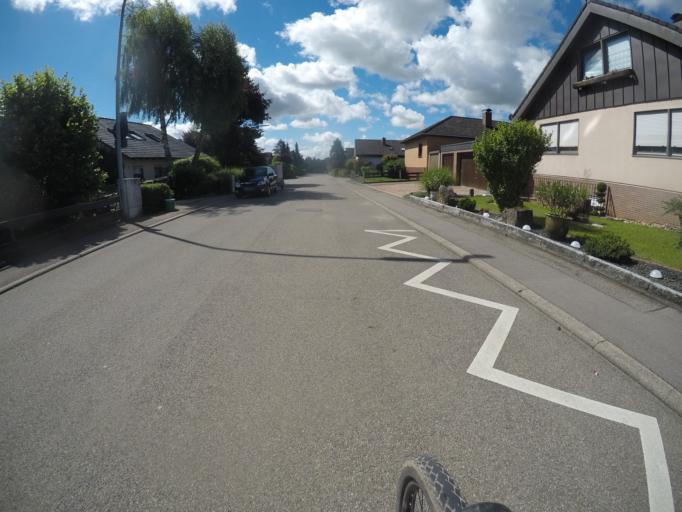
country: DE
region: Baden-Wuerttemberg
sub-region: Regierungsbezirk Stuttgart
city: Unterjettingen
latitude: 48.5622
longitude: 8.7856
